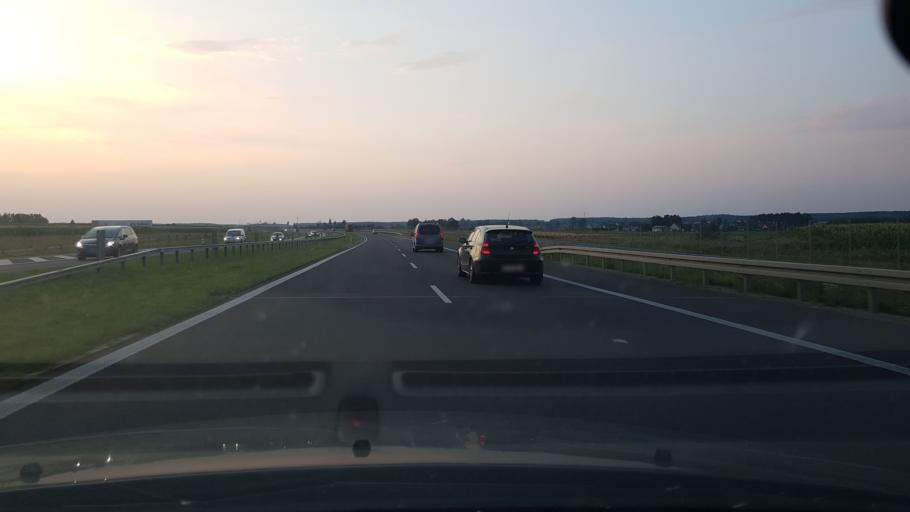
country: PL
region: Masovian Voivodeship
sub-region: Powiat mlawski
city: Wieczfnia Koscielna
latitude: 53.2149
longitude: 20.4293
